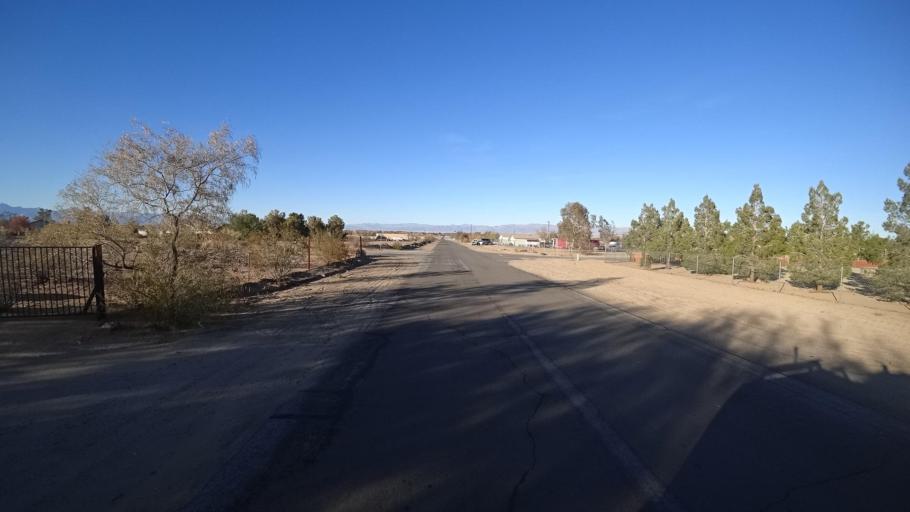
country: US
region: California
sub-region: Kern County
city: Ridgecrest
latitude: 35.5967
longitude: -117.6617
